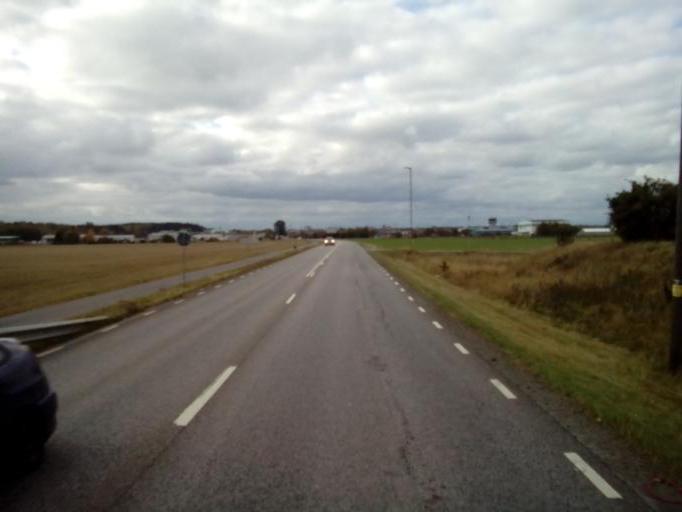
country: SE
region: OEstergoetland
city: Lindo
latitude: 58.5817
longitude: 16.2493
